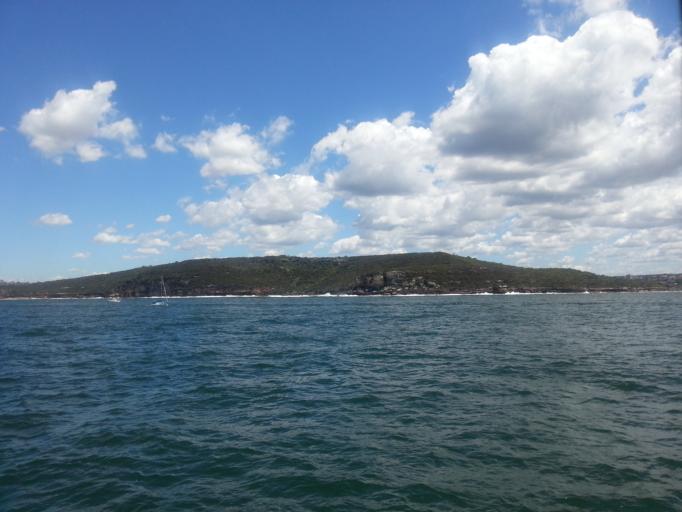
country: AU
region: New South Wales
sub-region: Manly Vale
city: Manly
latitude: -33.8162
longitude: 151.2796
